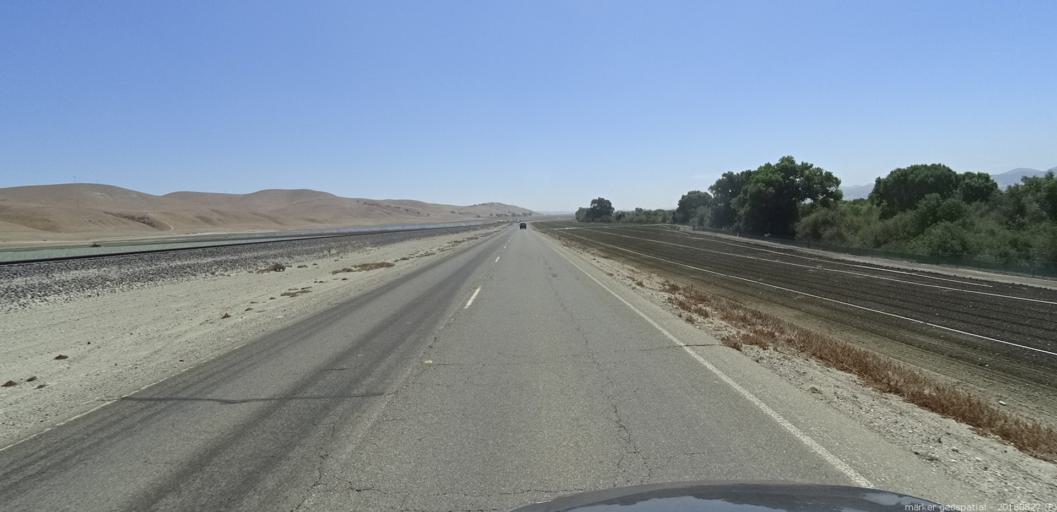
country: US
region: California
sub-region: Monterey County
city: King City
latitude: 36.0632
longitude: -120.9289
